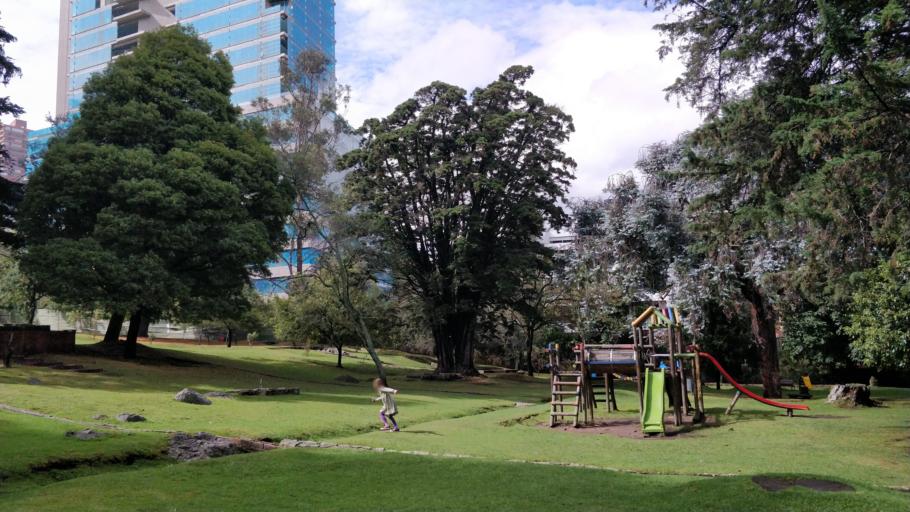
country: CO
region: Bogota D.C.
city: Barrio San Luis
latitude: 4.6731
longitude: -74.0444
